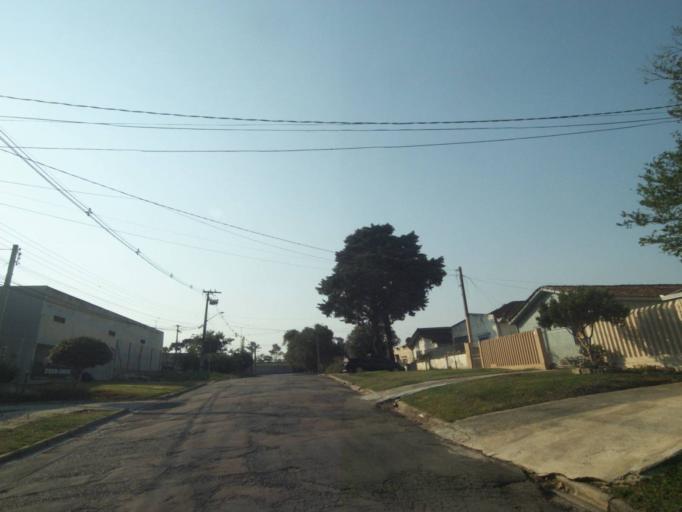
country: BR
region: Parana
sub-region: Curitiba
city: Curitiba
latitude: -25.4908
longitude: -49.2694
